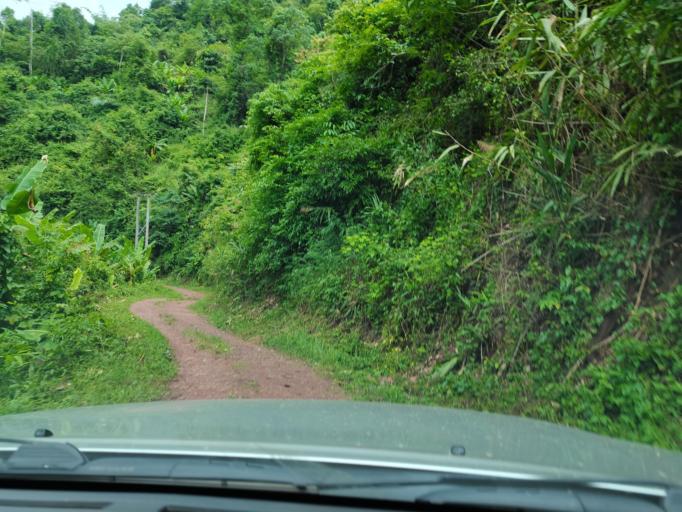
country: LA
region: Loungnamtha
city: Muang Nale
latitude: 20.5155
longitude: 101.0760
